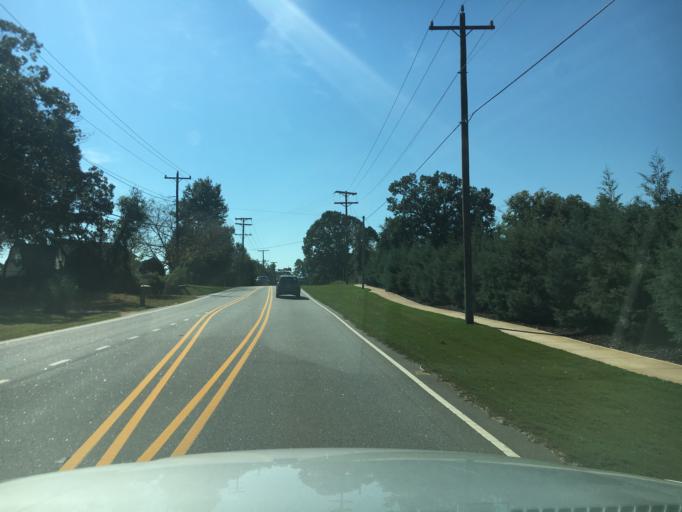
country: US
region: South Carolina
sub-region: Greenville County
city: Taylors
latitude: 34.9290
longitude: -82.2690
